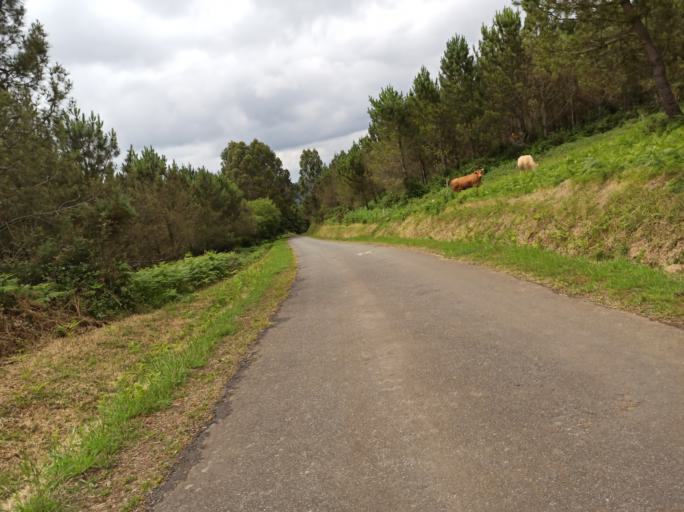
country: ES
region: Galicia
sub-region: Provincia de Pontevedra
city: Silleda
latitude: 42.7678
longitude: -8.1619
